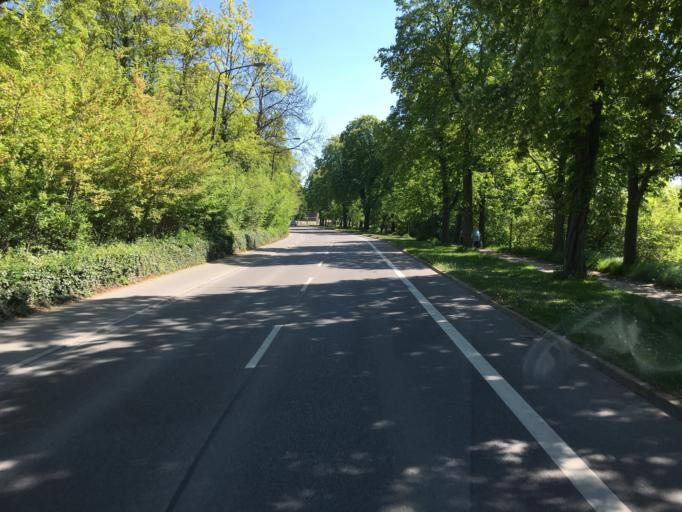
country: DE
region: Saxony-Anhalt
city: Naumburg
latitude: 51.1576
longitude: 11.7987
